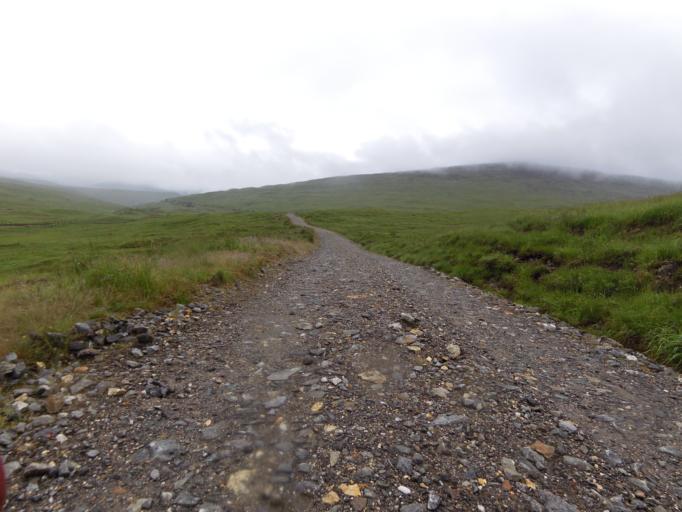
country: GB
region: Scotland
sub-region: Highland
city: Spean Bridge
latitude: 56.7726
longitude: -4.7058
